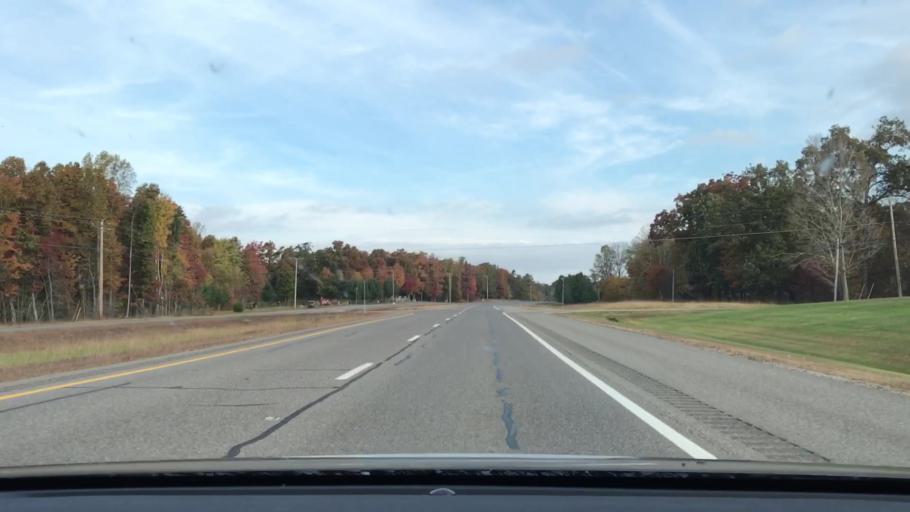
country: US
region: Tennessee
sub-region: Fentress County
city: Jamestown
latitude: 36.3727
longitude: -84.9440
